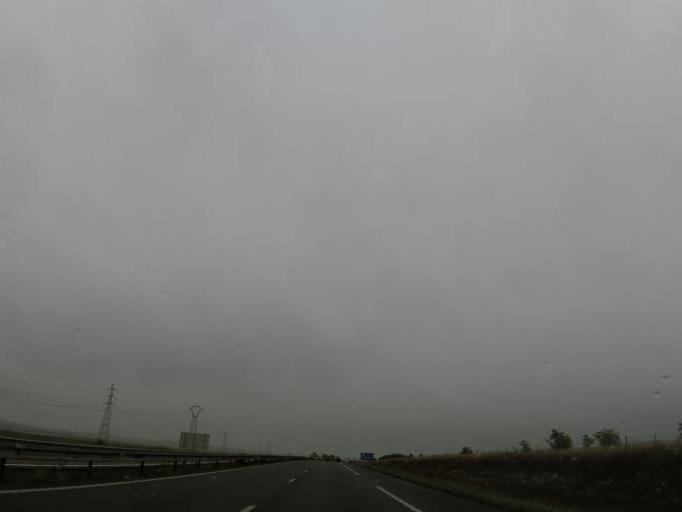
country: FR
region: Champagne-Ardenne
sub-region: Departement de la Marne
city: Taissy
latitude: 49.2019
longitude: 4.1001
